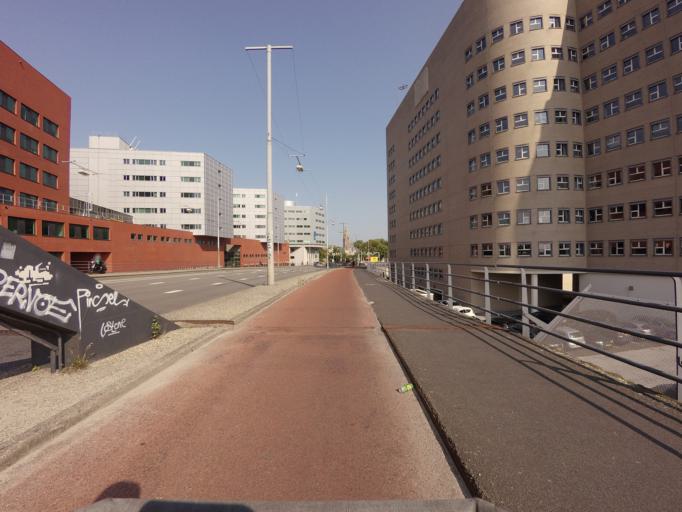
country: NL
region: Groningen
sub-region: Gemeente Groningen
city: Groningen
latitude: 53.2108
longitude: 6.5613
